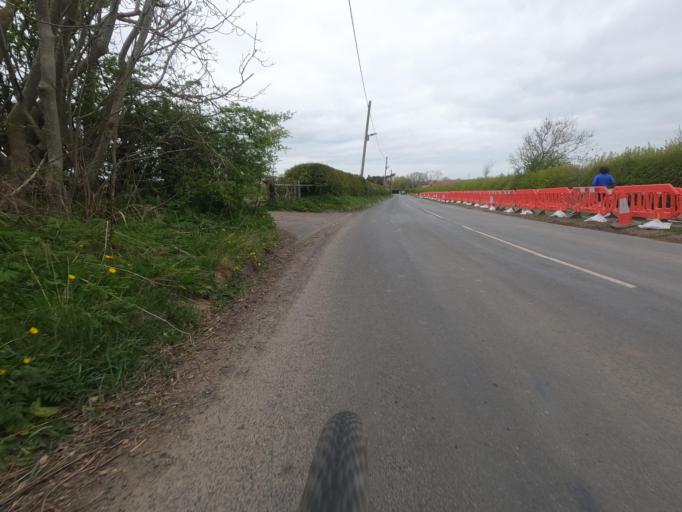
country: GB
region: England
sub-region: Northumberland
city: Ponteland
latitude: 55.0576
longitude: -1.7491
